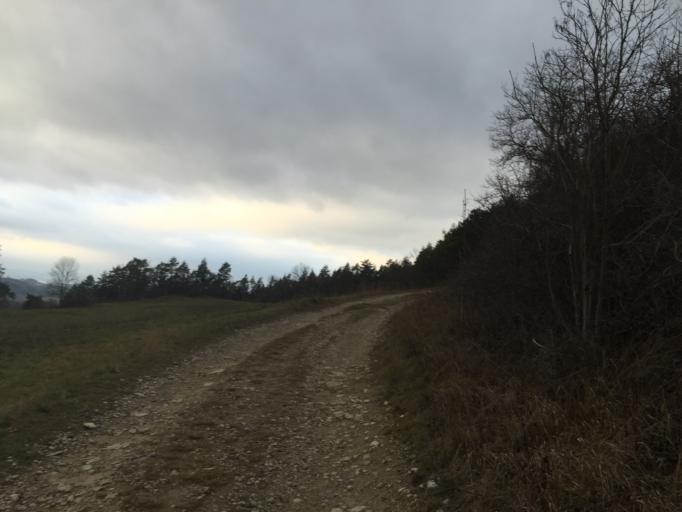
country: DE
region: Thuringia
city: Bad Blankenburg
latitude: 50.7020
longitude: 11.2472
